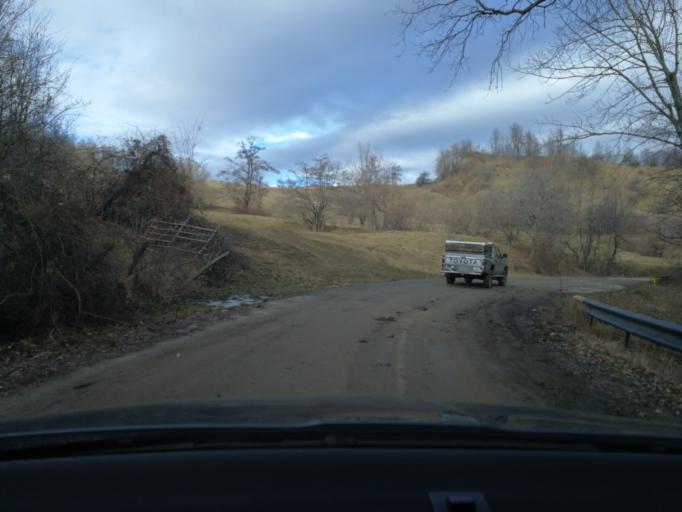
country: RO
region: Prahova
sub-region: Comuna Adunati
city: Ocina de Sus
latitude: 45.1754
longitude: 25.5639
